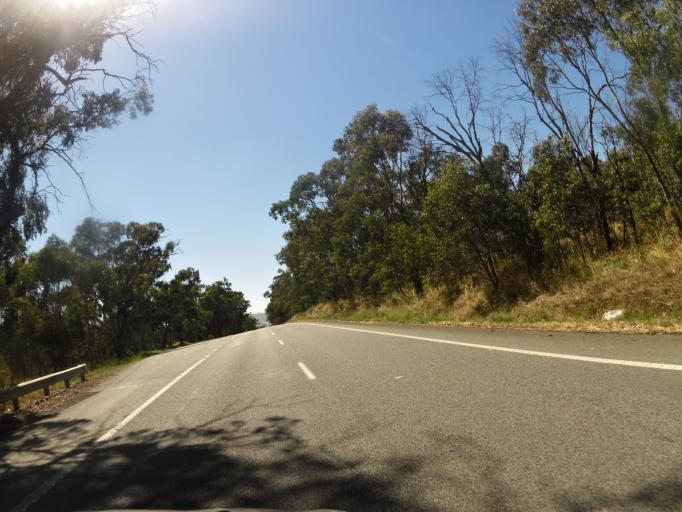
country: AU
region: Victoria
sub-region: Greater Shepparton
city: Shepparton
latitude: -36.7707
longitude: 145.5244
